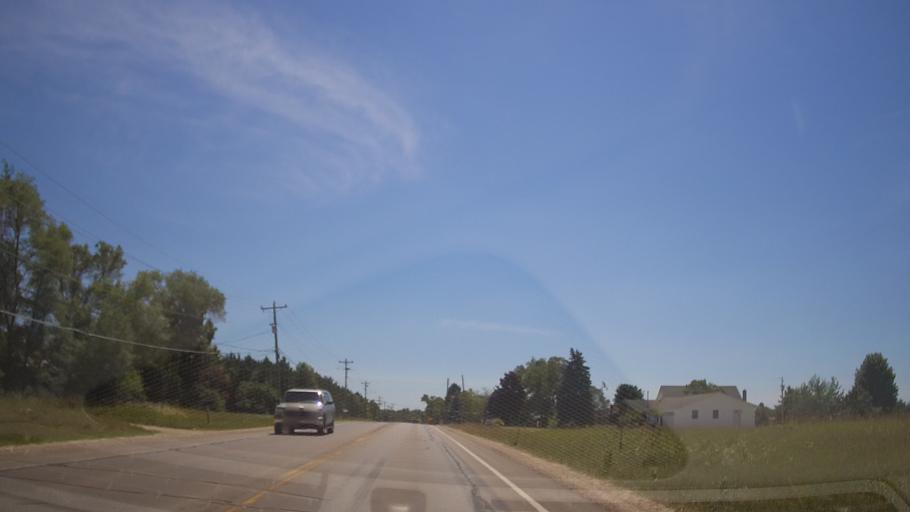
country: US
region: Michigan
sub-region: Grand Traverse County
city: Traverse City
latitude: 44.6697
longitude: -85.6901
